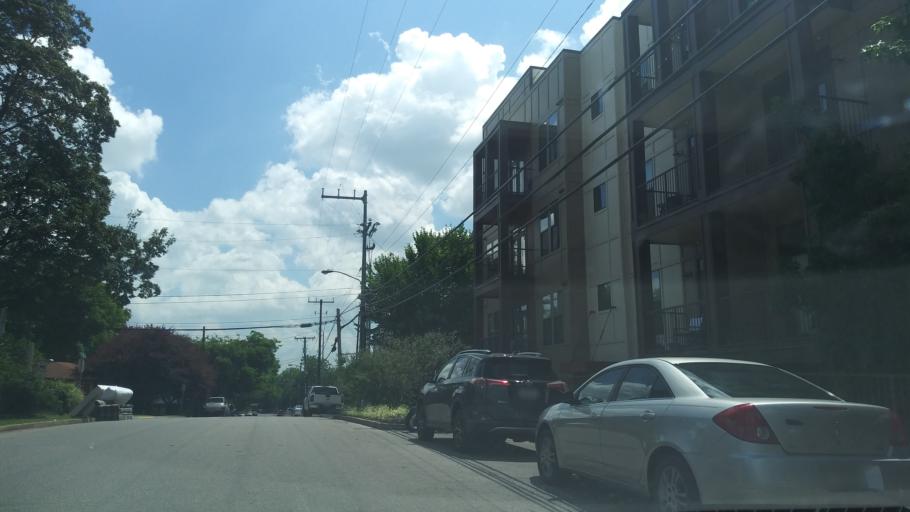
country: US
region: Tennessee
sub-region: Davidson County
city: Nashville
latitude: 36.1288
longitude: -86.7771
